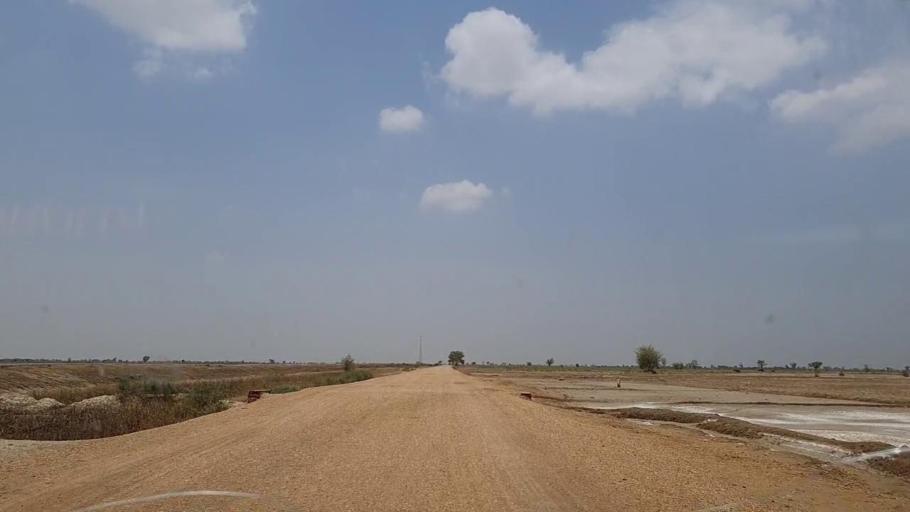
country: PK
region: Sindh
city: Johi
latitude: 26.7736
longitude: 67.6550
